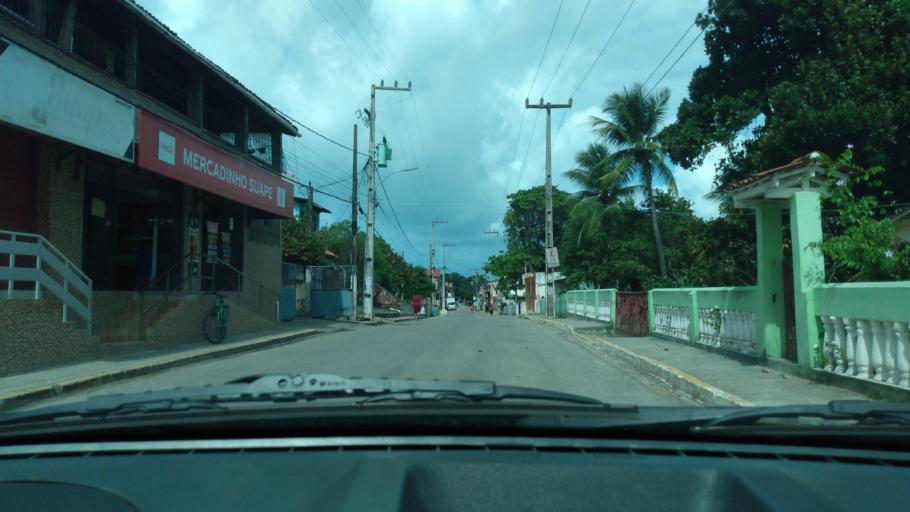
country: BR
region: Pernambuco
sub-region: Cabo De Santo Agostinho
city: Cabo
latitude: -8.3532
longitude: -34.9563
